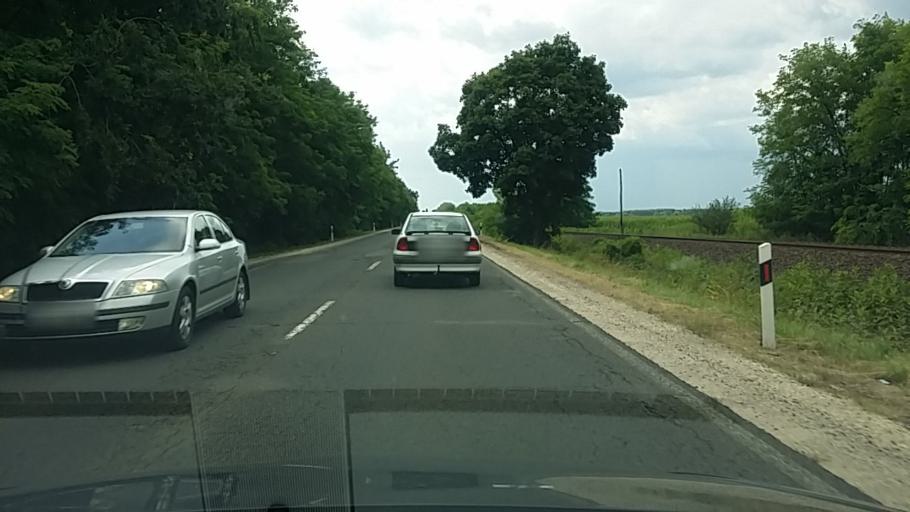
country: HU
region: Pest
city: Ujhartyan
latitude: 47.1662
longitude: 19.3756
